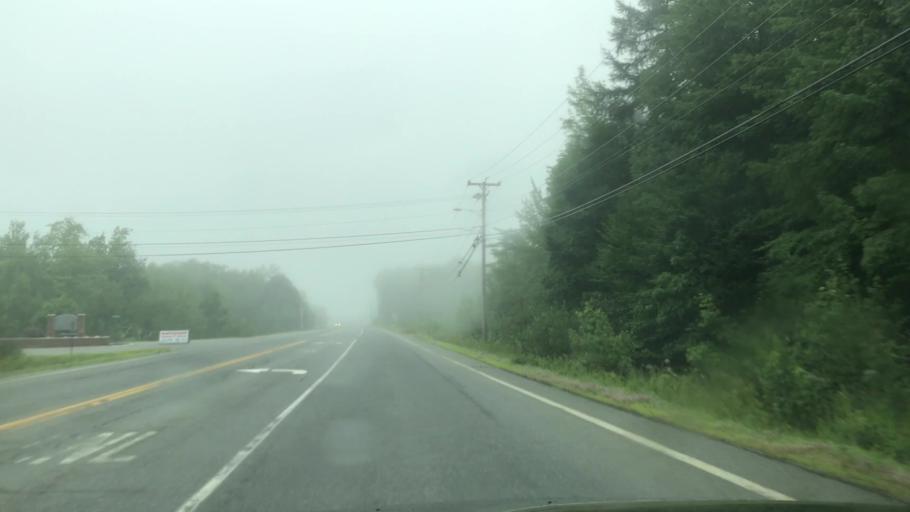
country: US
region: Maine
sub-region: Knox County
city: Rockport
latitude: 44.1857
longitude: -69.1011
